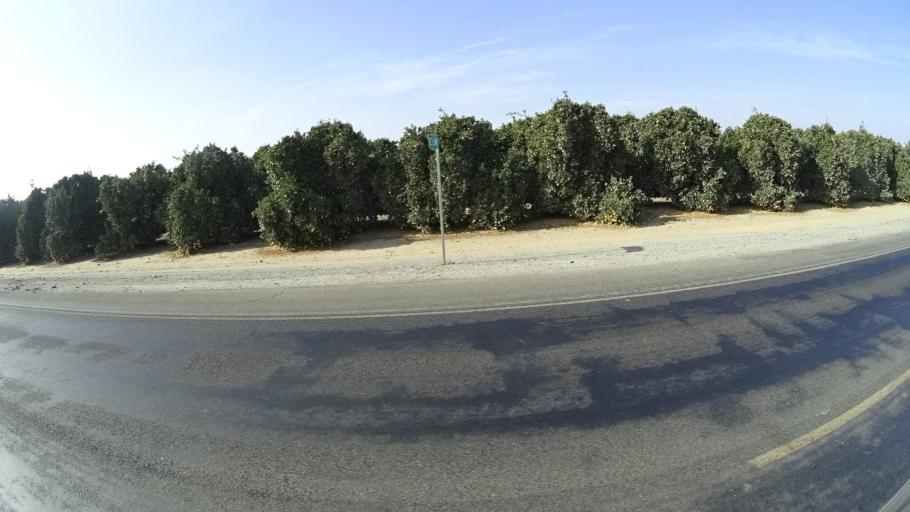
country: US
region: California
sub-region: Kern County
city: McFarland
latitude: 35.6901
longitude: -119.1769
